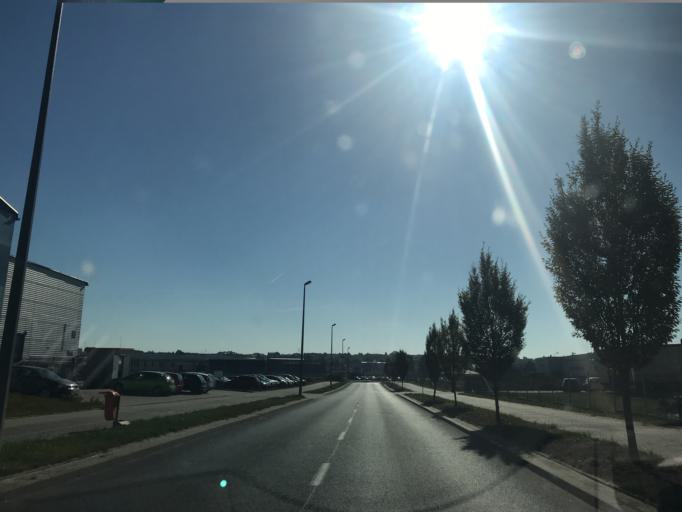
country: PL
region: Warmian-Masurian Voivodeship
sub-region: Powiat ilawski
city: Lubawa
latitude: 53.5142
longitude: 19.7359
